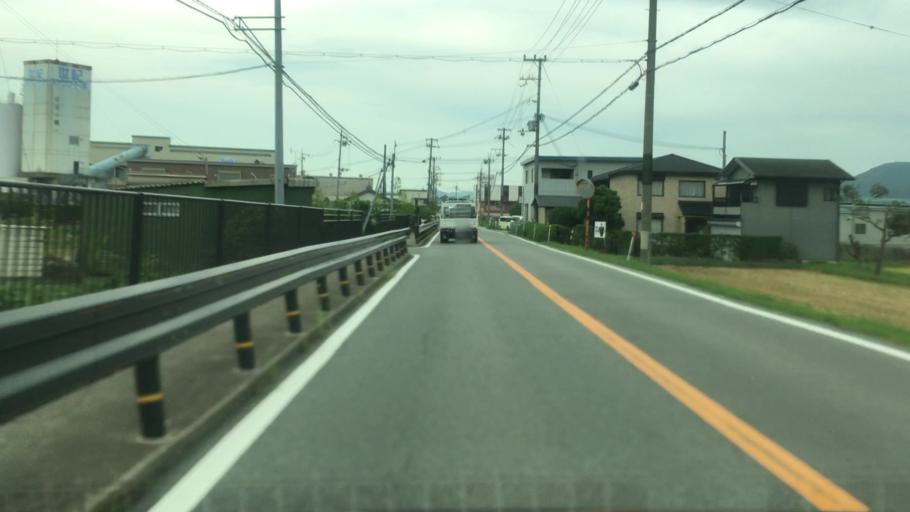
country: JP
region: Hyogo
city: Sasayama
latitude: 35.0671
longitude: 135.2422
